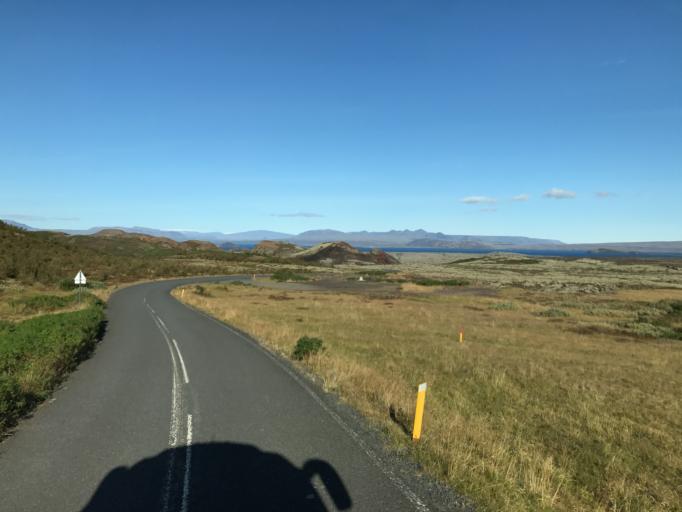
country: IS
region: South
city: Hveragerdi
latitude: 64.1204
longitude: -21.2587
